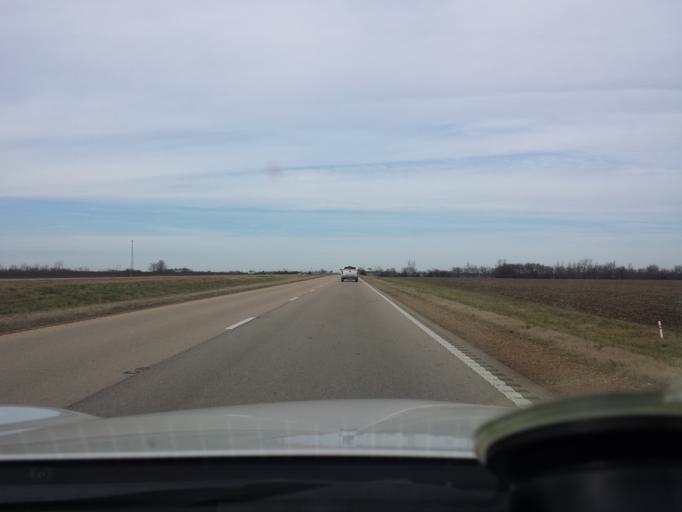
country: US
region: Mississippi
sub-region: Monroe County
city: Aberdeen
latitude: 33.8266
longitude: -88.7067
